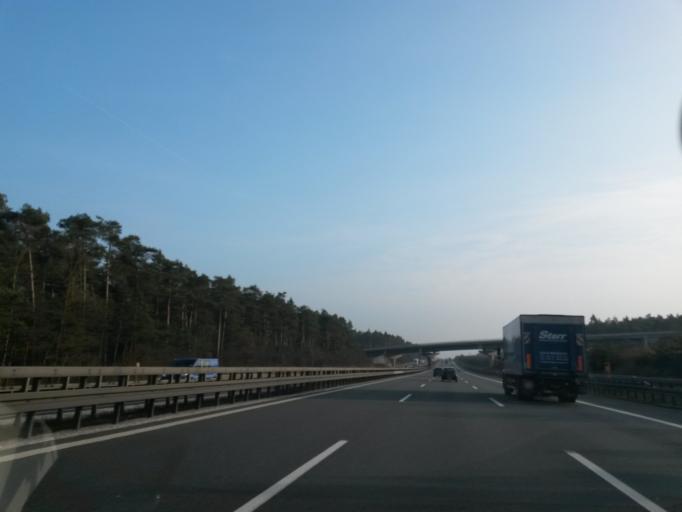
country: DE
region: Bavaria
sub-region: Regierungsbezirk Mittelfranken
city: Schwarzenbruck
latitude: 49.3121
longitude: 11.2074
